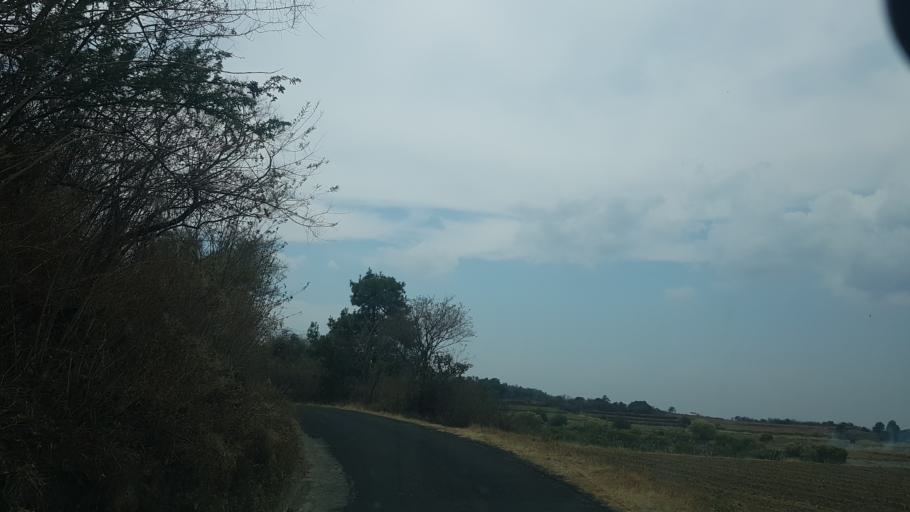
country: MX
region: Puebla
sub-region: Atzitzihuacan
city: Santiago Atzitzihuacan
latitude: 18.8456
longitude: -98.6091
